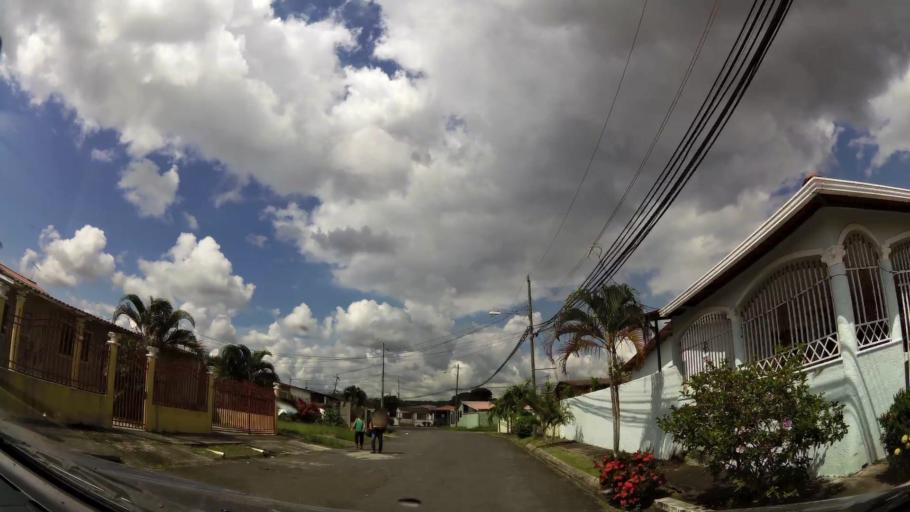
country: PA
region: Panama
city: Nuevo Arraijan
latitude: 8.9298
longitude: -79.7271
